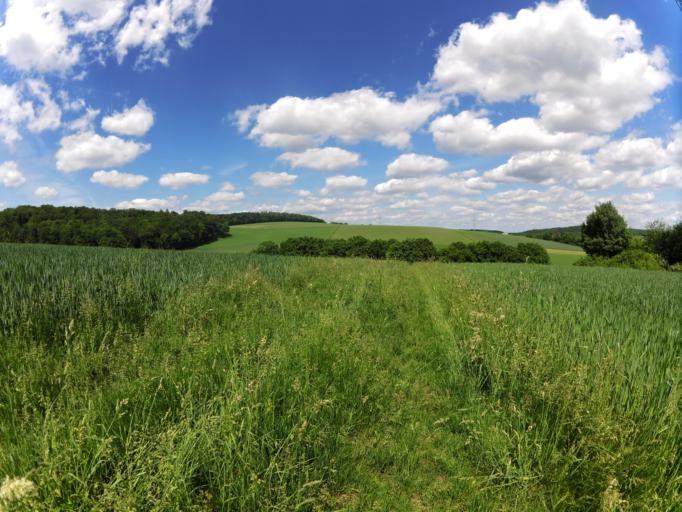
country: DE
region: Bavaria
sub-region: Regierungsbezirk Unterfranken
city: Waldbrunn
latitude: 49.7716
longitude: 9.7697
